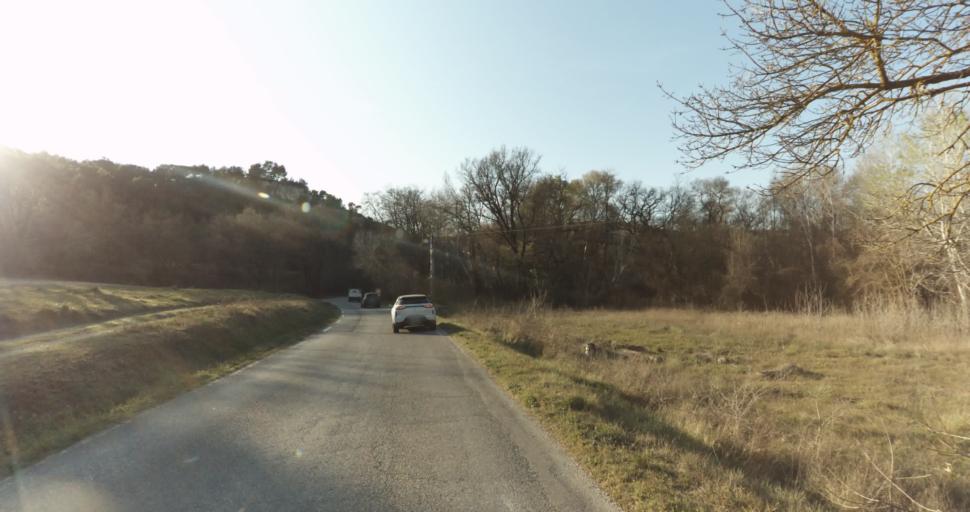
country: FR
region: Provence-Alpes-Cote d'Azur
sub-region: Departement des Bouches-du-Rhone
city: Ventabren
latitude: 43.5140
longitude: 5.3201
